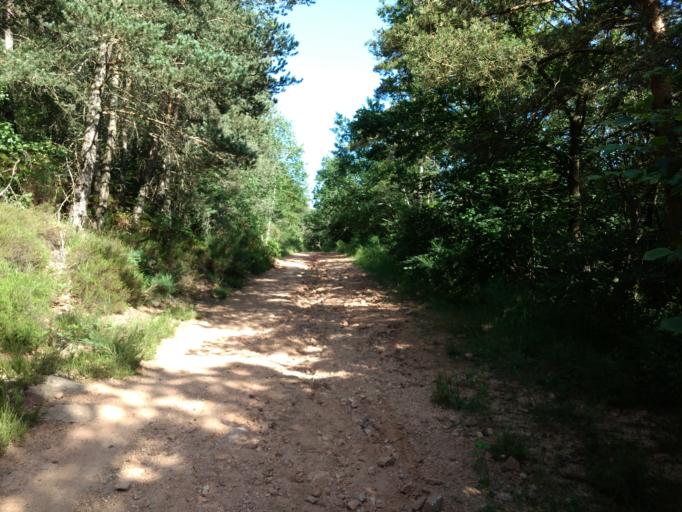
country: FR
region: Midi-Pyrenees
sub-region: Departement de l'Aveyron
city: La Loubiere
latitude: 44.3581
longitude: 2.6997
